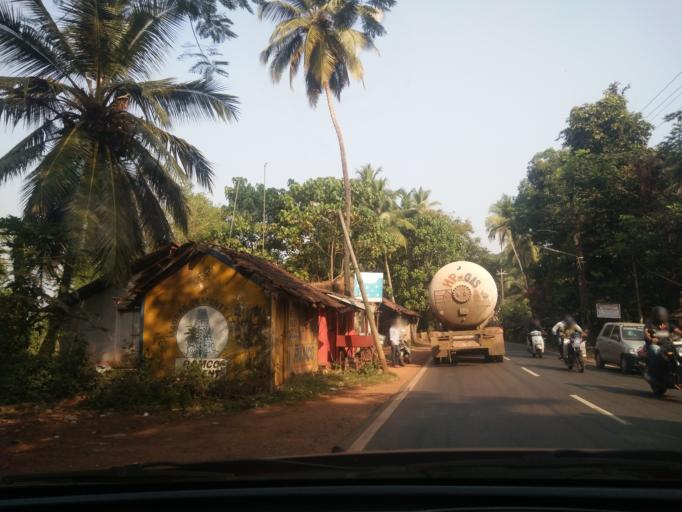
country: IN
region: Goa
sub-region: North Goa
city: Queula
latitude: 15.3550
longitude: 74.0028
